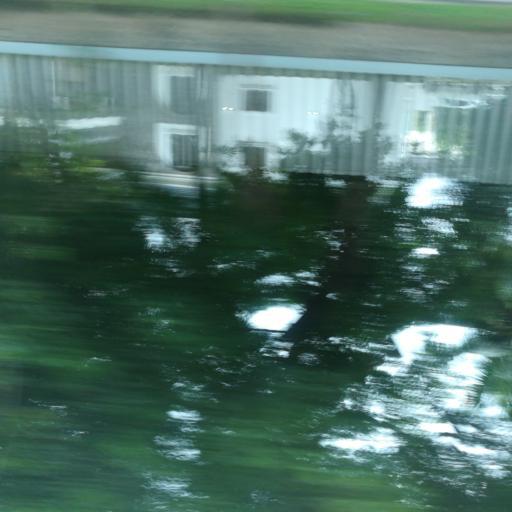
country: NG
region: Lagos
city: Ikoyi
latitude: 6.4553
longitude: 3.4465
